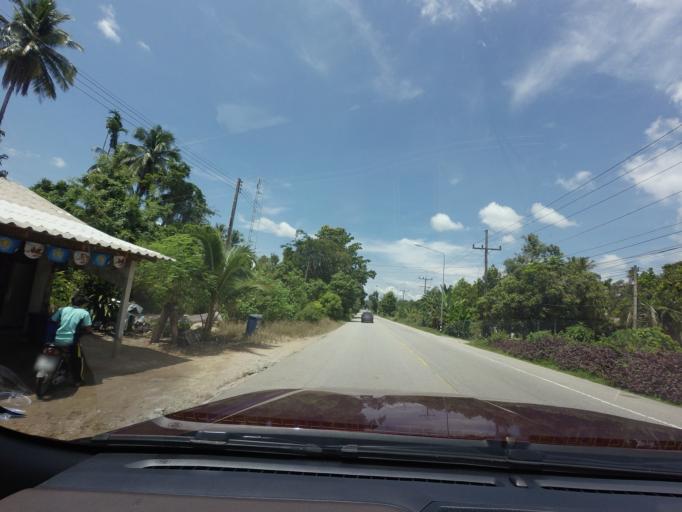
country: TH
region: Narathiwat
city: Chanae
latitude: 6.1970
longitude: 101.6869
